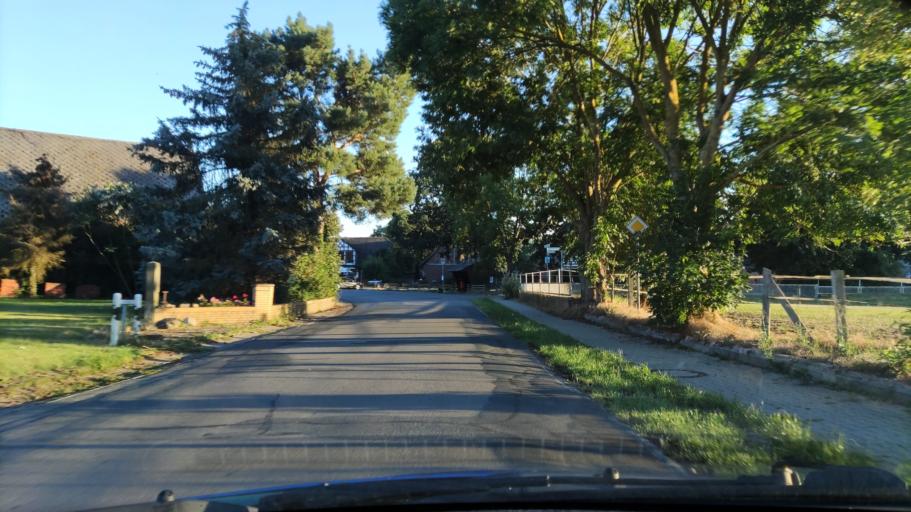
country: DE
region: Lower Saxony
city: Luechow
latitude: 53.0010
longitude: 11.1510
